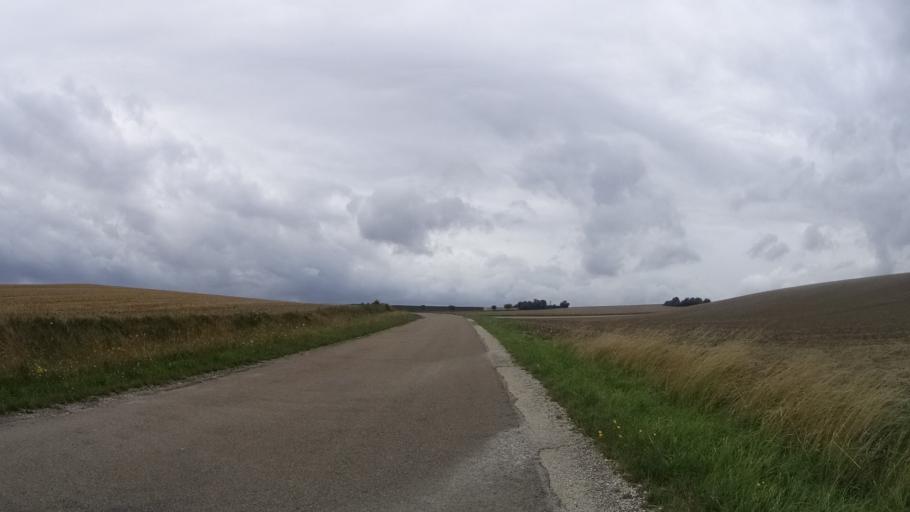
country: FR
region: Champagne-Ardenne
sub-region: Departement de l'Aube
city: Bouilly
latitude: 48.1463
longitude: 4.0374
